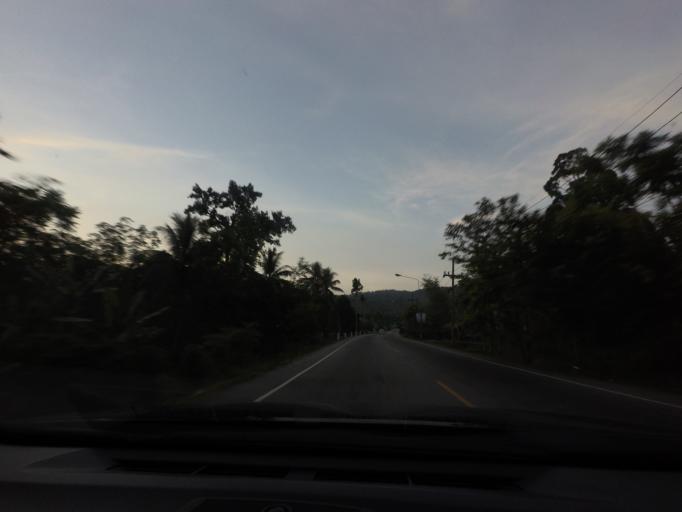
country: TH
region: Narathiwat
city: Rueso
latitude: 6.3701
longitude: 101.5563
